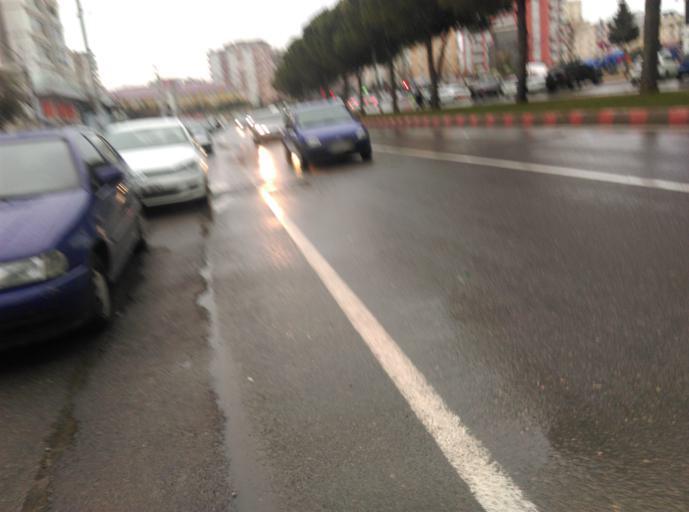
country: TR
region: Kahramanmaras
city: Kahramanmaras
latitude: 37.5840
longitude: 36.8888
